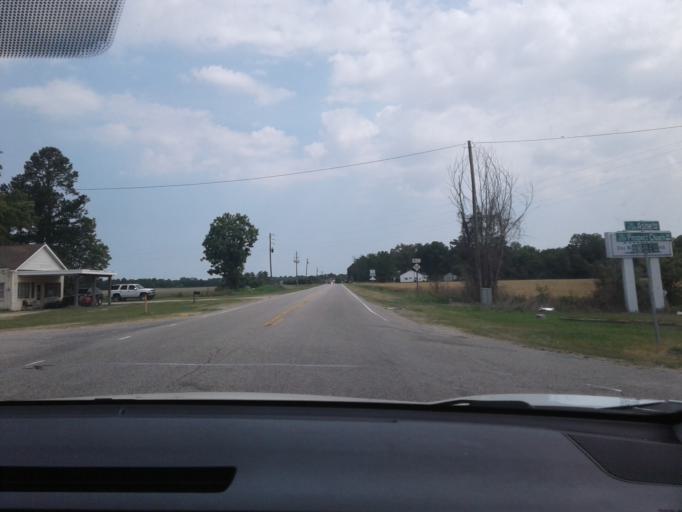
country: US
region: North Carolina
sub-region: Harnett County
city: Erwin
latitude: 35.3635
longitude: -78.6636
